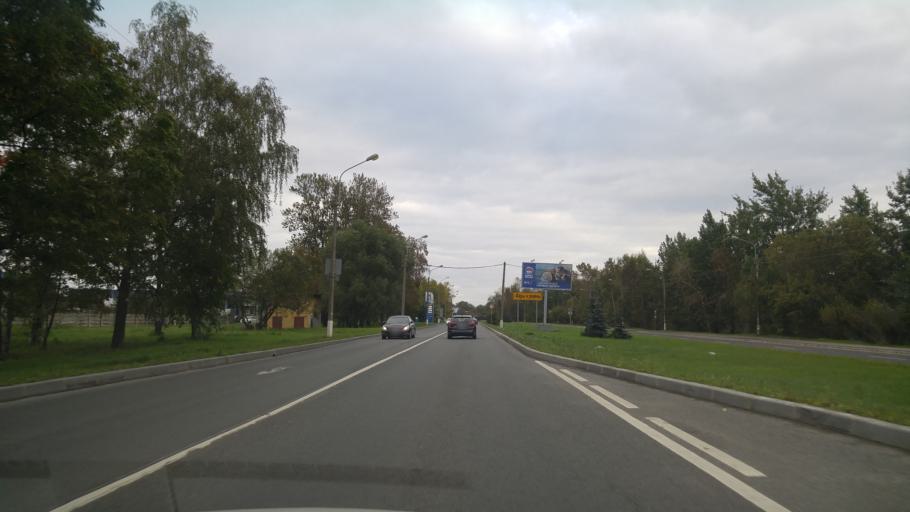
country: RU
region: St.-Petersburg
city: Kronshtadt
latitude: 60.0087
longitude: 29.7341
